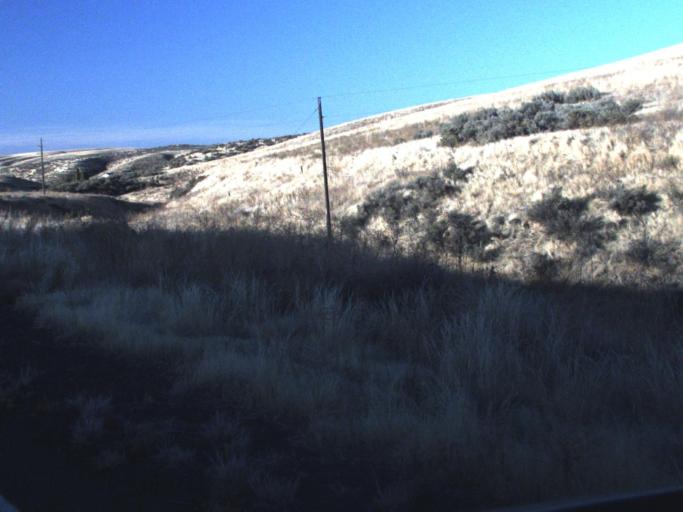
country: US
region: Washington
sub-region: Adams County
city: Ritzville
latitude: 46.6876
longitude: -118.3879
